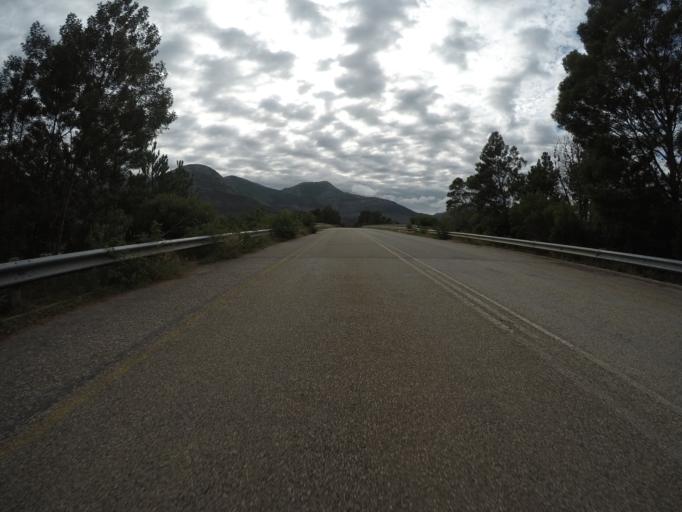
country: ZA
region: Eastern Cape
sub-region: Cacadu District Municipality
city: Kareedouw
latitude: -34.0139
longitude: 24.3065
